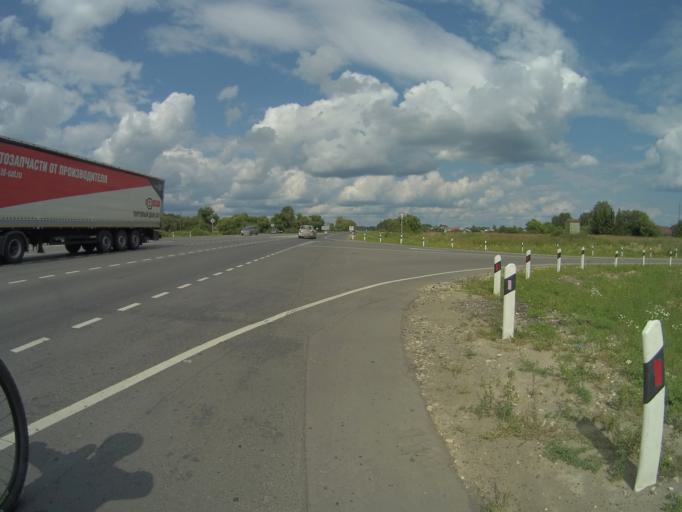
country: RU
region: Vladimir
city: Kideksha
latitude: 56.5583
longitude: 40.5482
